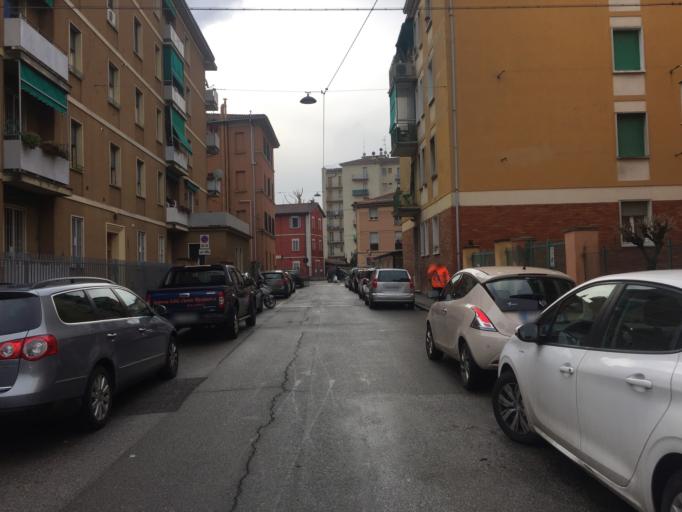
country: IT
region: Emilia-Romagna
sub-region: Provincia di Bologna
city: Bologna
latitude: 44.5086
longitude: 11.3017
